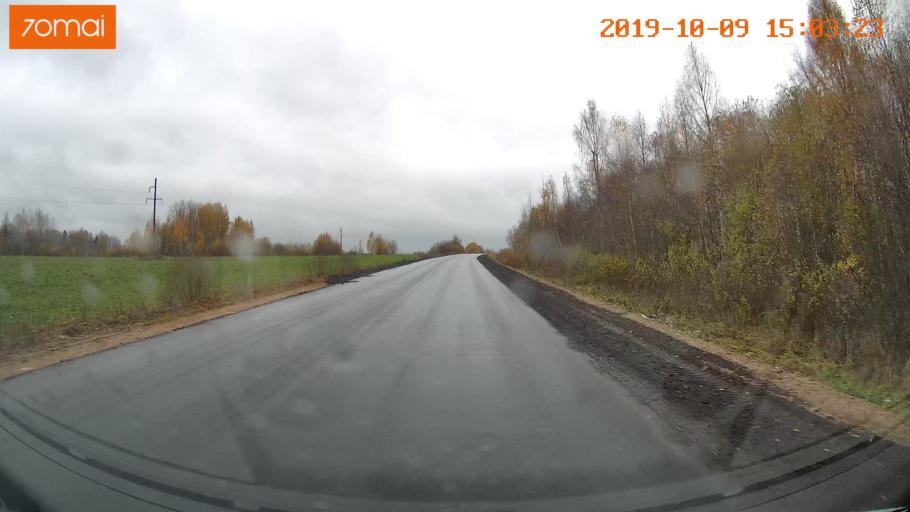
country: RU
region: Kostroma
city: Chistyye Bory
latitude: 58.2719
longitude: 41.6759
